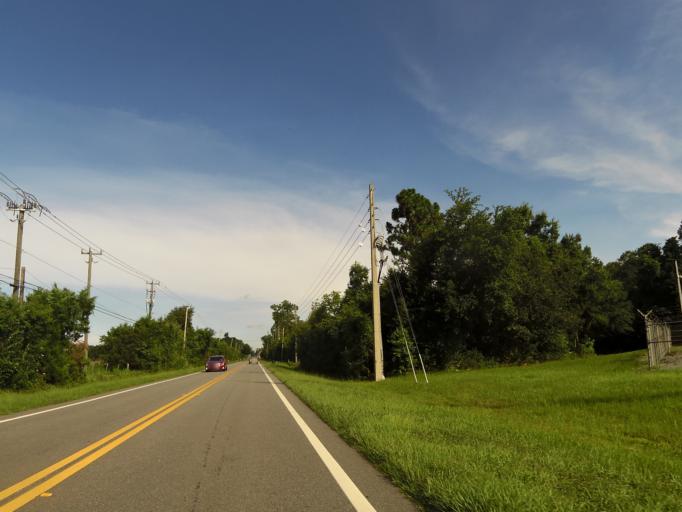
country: US
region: Florida
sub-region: Clay County
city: Green Cove Springs
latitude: 29.9889
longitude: -81.5306
